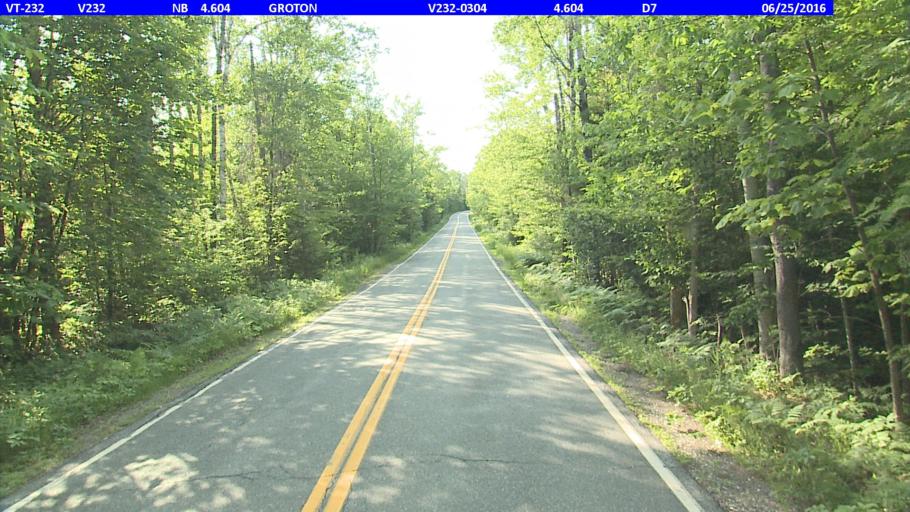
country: US
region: Vermont
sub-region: Washington County
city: Barre
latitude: 44.2682
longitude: -72.2765
